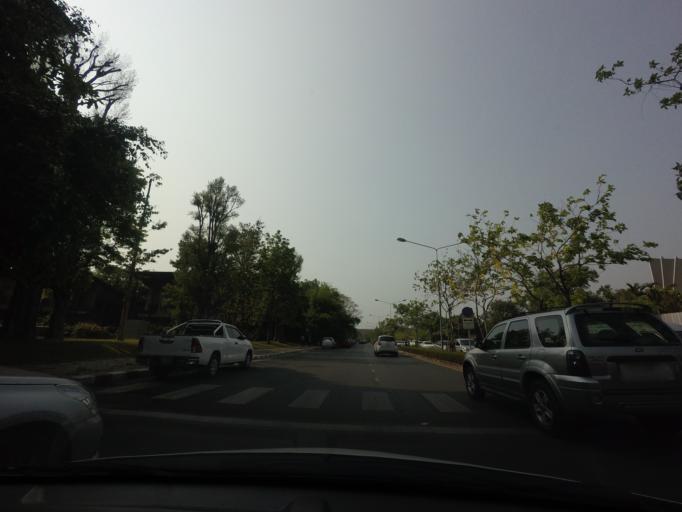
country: TH
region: Bangkok
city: Thawi Watthana
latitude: 13.7903
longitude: 100.3226
